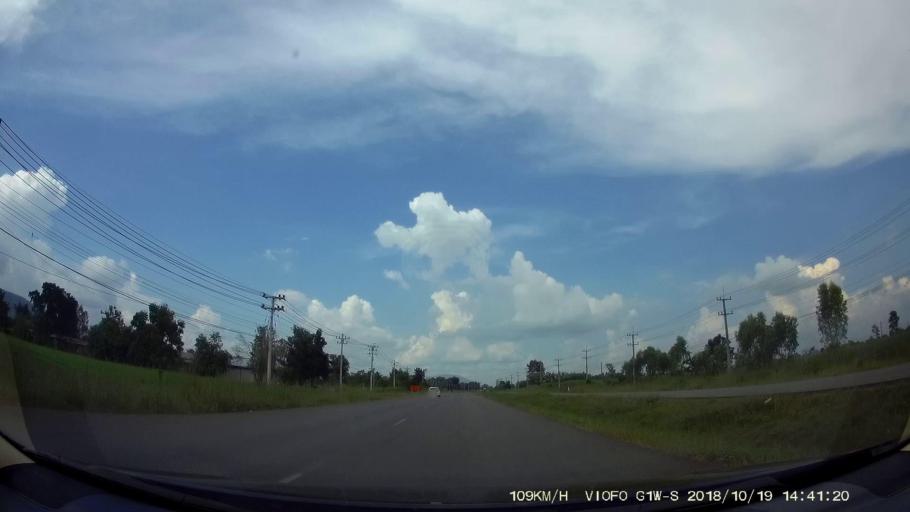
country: TH
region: Chaiyaphum
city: Phu Khiao
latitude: 16.2553
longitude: 102.1988
